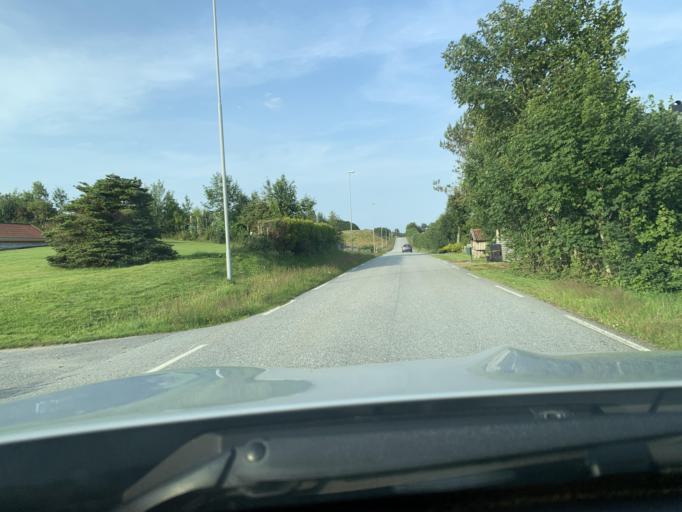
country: NO
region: Rogaland
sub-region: Time
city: Bryne
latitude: 58.7353
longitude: 5.6024
